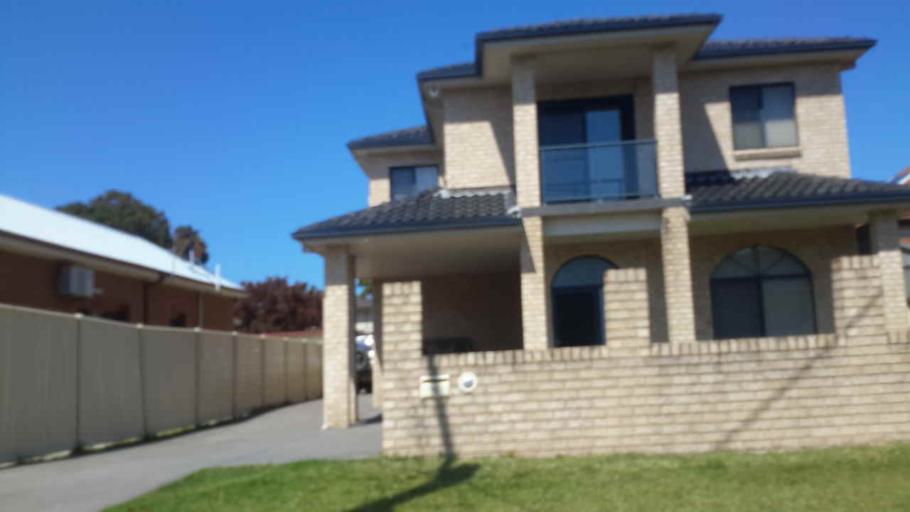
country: AU
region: New South Wales
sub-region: Wollongong
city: Corrimal
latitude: -34.3844
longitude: 150.8959
